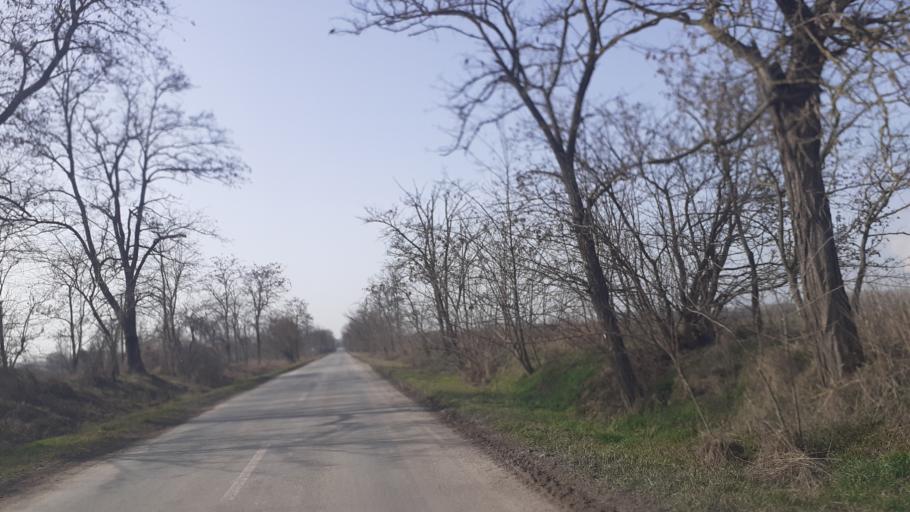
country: HU
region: Bacs-Kiskun
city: Tass
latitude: 47.0217
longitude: 18.9900
